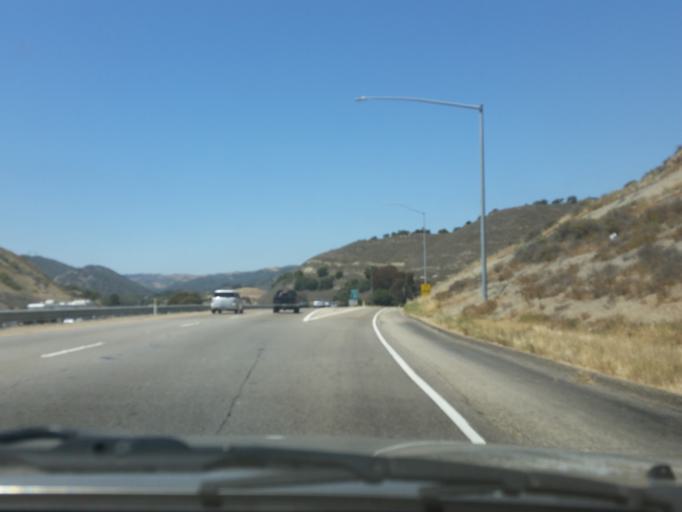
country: US
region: California
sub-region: San Luis Obispo County
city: Avila Beach
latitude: 35.1757
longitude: -120.6972
